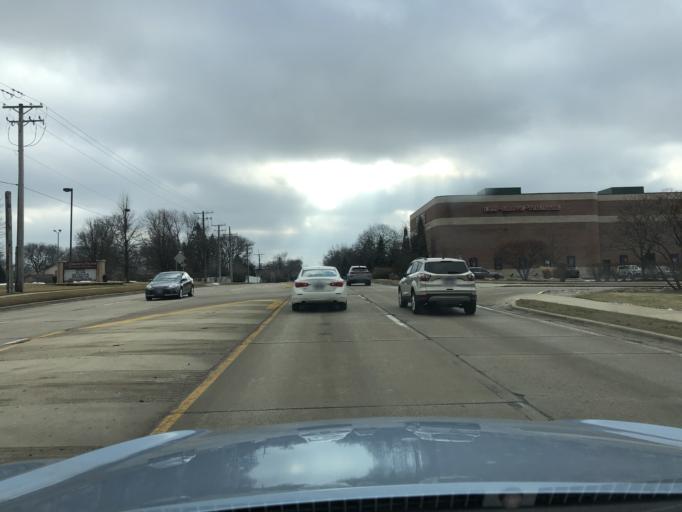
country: US
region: Illinois
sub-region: DuPage County
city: Itasca
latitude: 42.0011
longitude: -88.0038
